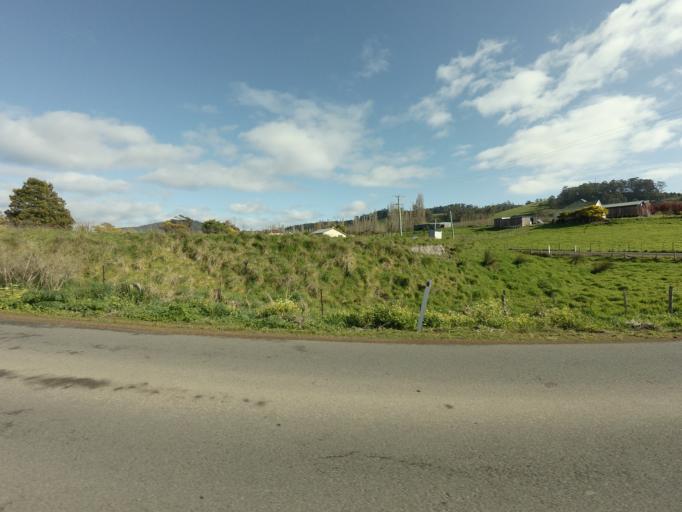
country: AU
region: Tasmania
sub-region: Huon Valley
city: Geeveston
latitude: -43.3204
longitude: 147.0071
